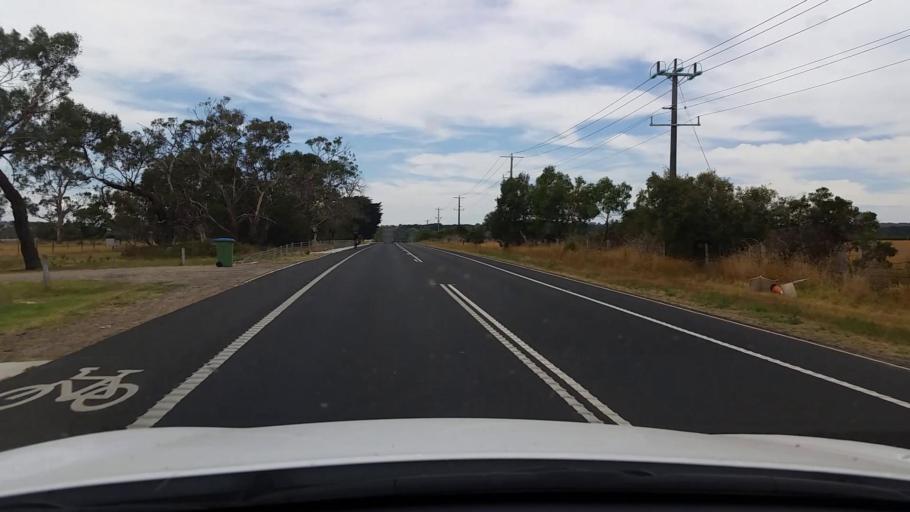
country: AU
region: Victoria
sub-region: Mornington Peninsula
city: Safety Beach
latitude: -38.3148
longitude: 145.0201
